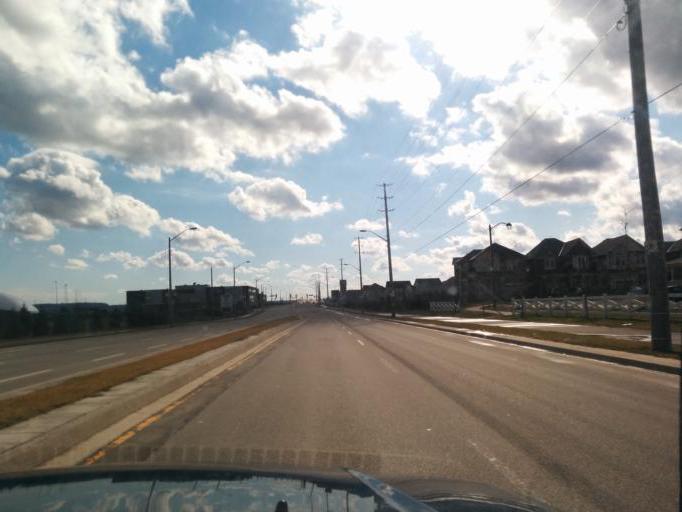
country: CA
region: Ontario
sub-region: Halton
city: Milton
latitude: 43.4907
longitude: -79.8546
